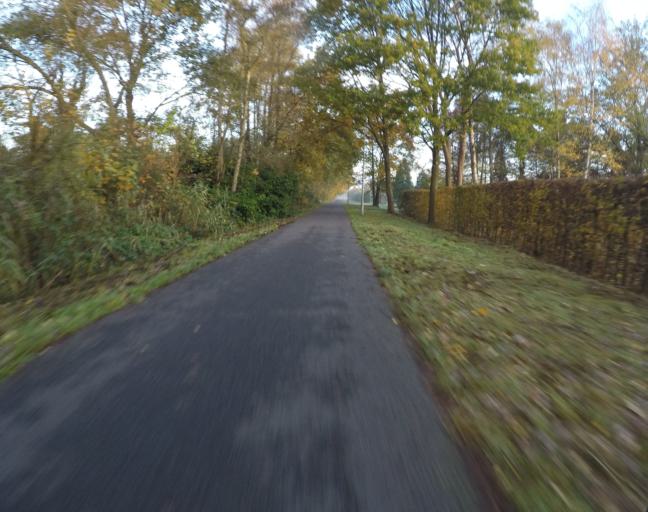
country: BE
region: Flanders
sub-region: Provincie Vlaams-Brabant
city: Begijnendijk
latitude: 51.0381
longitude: 4.8249
